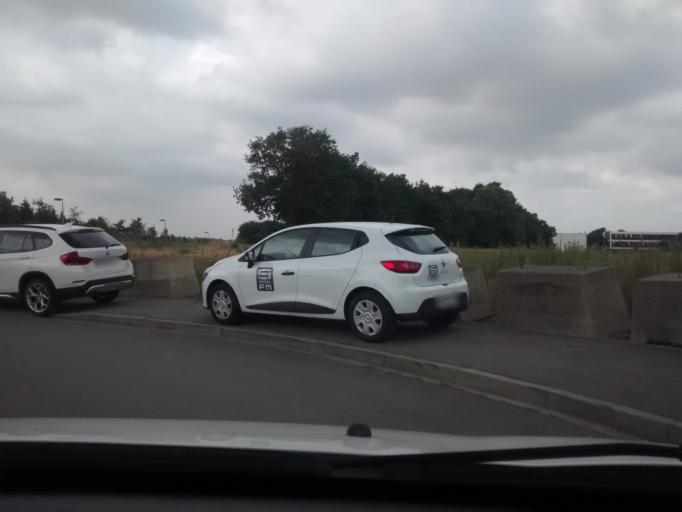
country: FR
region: Brittany
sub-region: Departement d'Ille-et-Vilaine
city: Cesson-Sevigne
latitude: 48.1133
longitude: -1.5829
